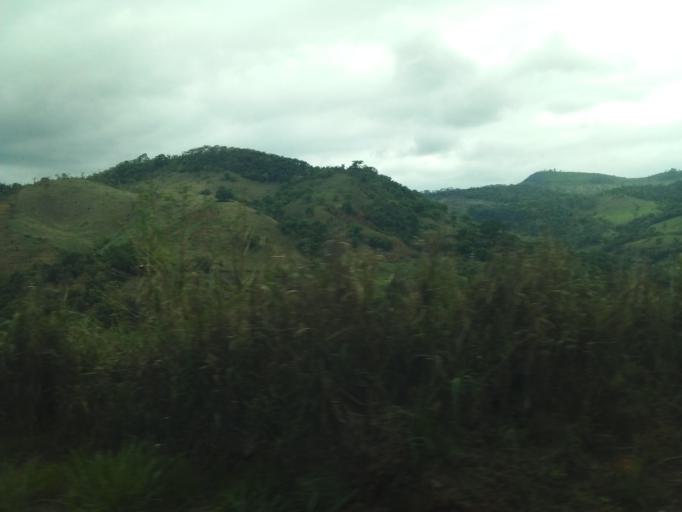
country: BR
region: Minas Gerais
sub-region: Nova Era
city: Nova Era
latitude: -19.6829
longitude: -42.9110
